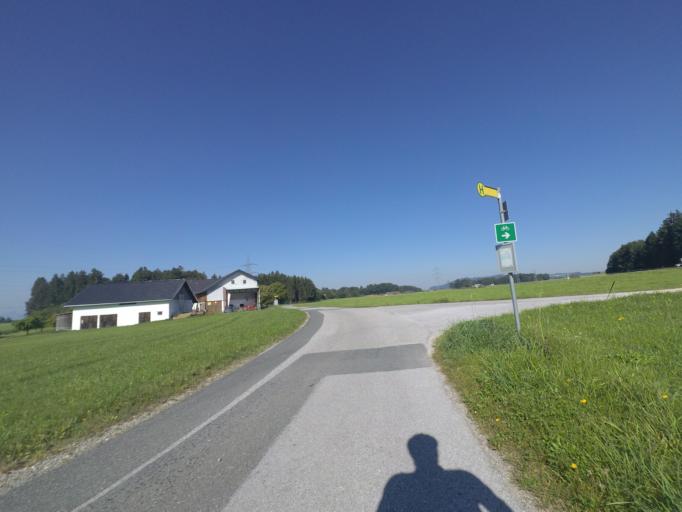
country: AT
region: Salzburg
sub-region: Politischer Bezirk Salzburg-Umgebung
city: Elixhausen
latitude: 47.8857
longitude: 13.0893
